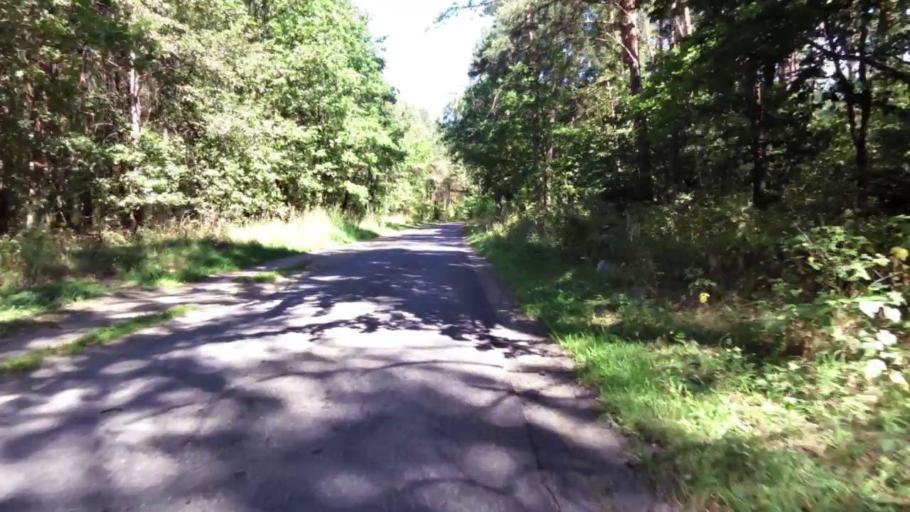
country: PL
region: West Pomeranian Voivodeship
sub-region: Powiat szczecinecki
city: Szczecinek
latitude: 53.6464
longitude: 16.7190
